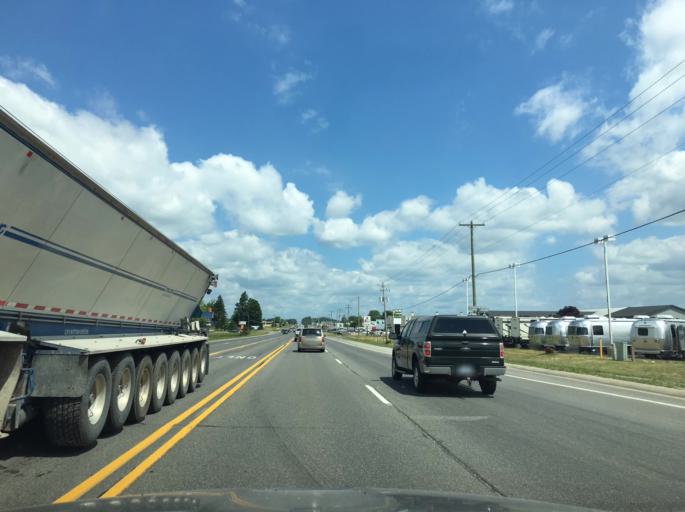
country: US
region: Michigan
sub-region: Grand Traverse County
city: Traverse City
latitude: 44.6865
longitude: -85.6562
